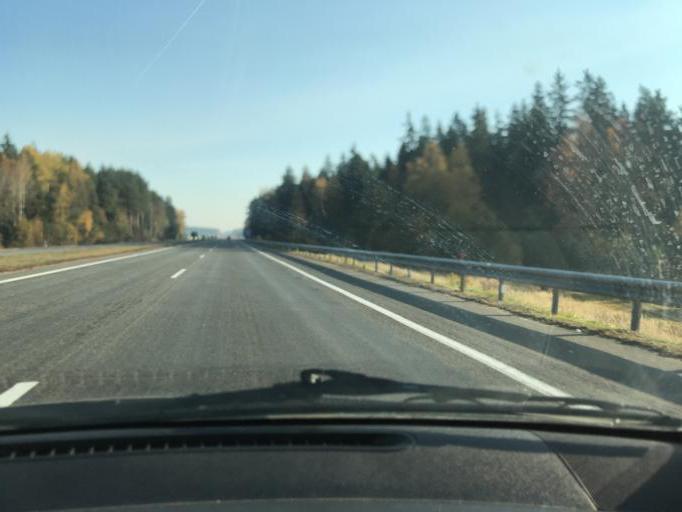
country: BY
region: Minsk
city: Horad Smalyavichy
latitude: 53.9575
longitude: 28.0006
